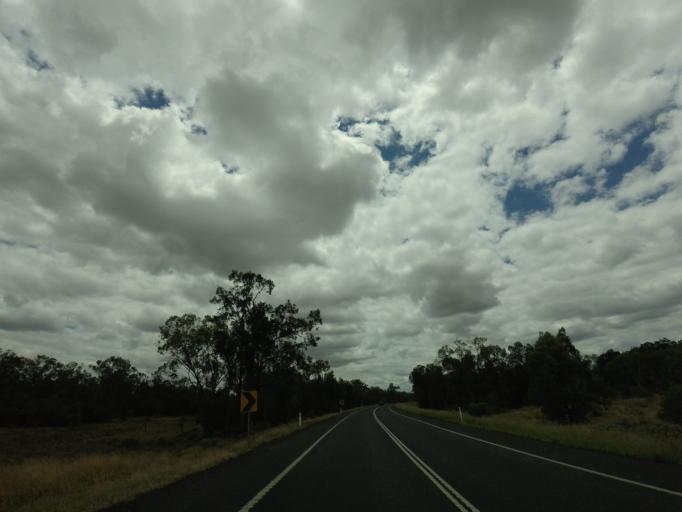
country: AU
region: Queensland
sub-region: Goondiwindi
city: Goondiwindi
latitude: -28.4033
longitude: 150.3068
